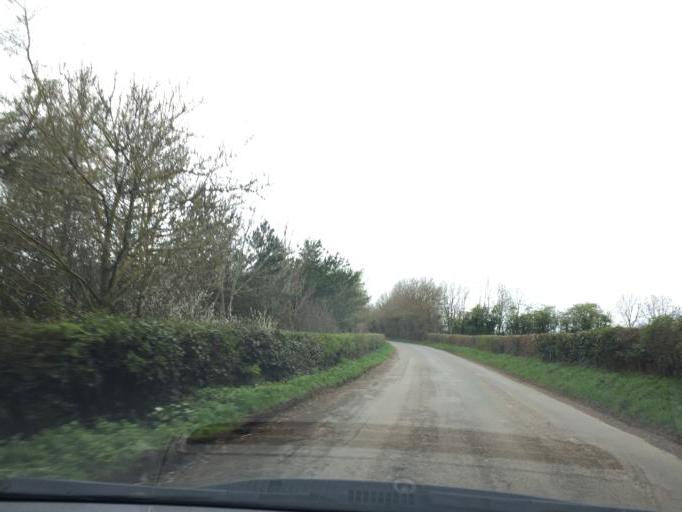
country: GB
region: England
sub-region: Oxfordshire
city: Hanwell
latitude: 52.1005
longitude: -1.4039
